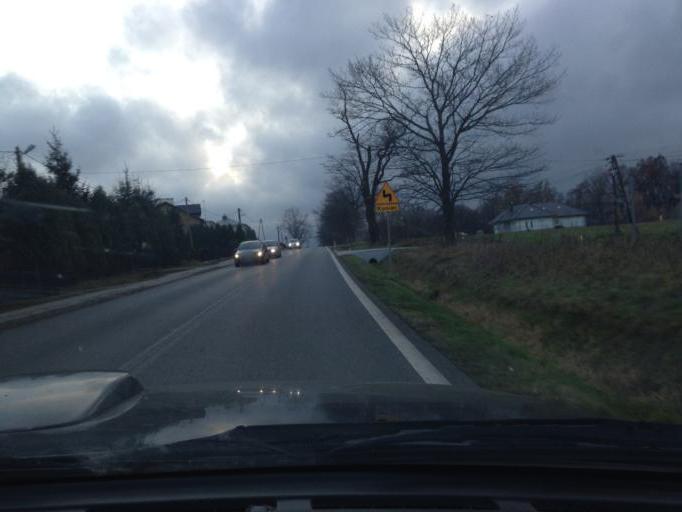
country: PL
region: Subcarpathian Voivodeship
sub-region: Powiat jasielski
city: Nowy Zmigrod
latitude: 49.6190
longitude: 21.5390
